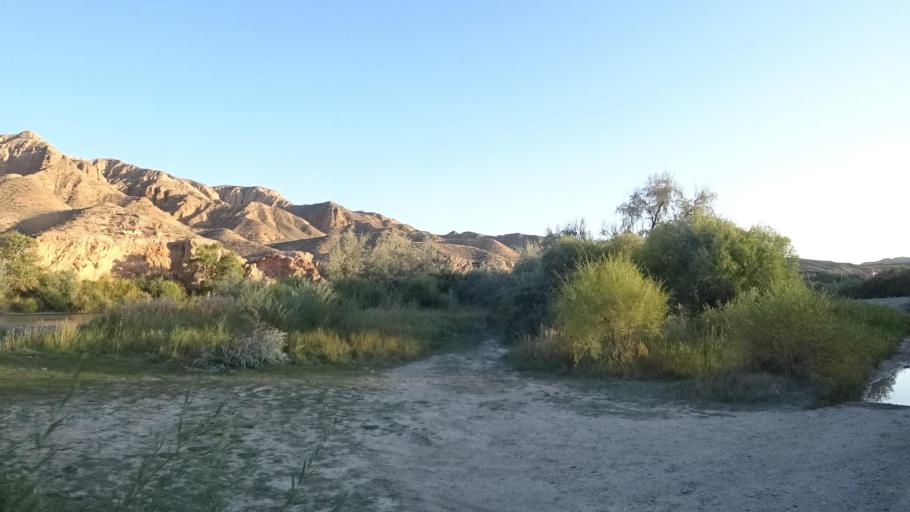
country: KZ
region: Almaty Oblysy
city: Kegen
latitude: 43.2728
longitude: 78.9774
